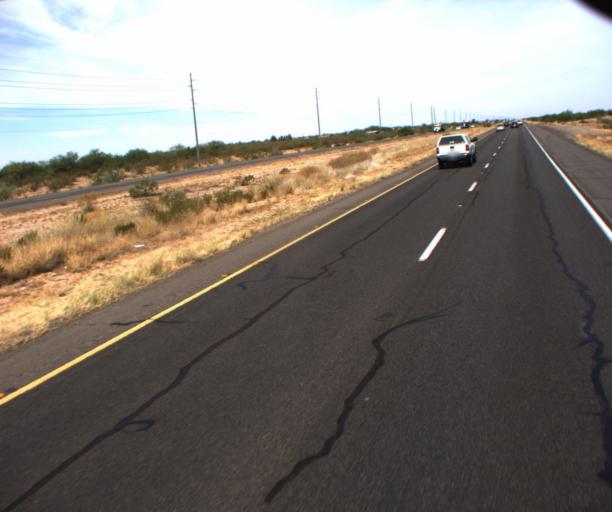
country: US
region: Arizona
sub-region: Maricopa County
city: Sun City West
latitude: 33.6991
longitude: -112.4275
